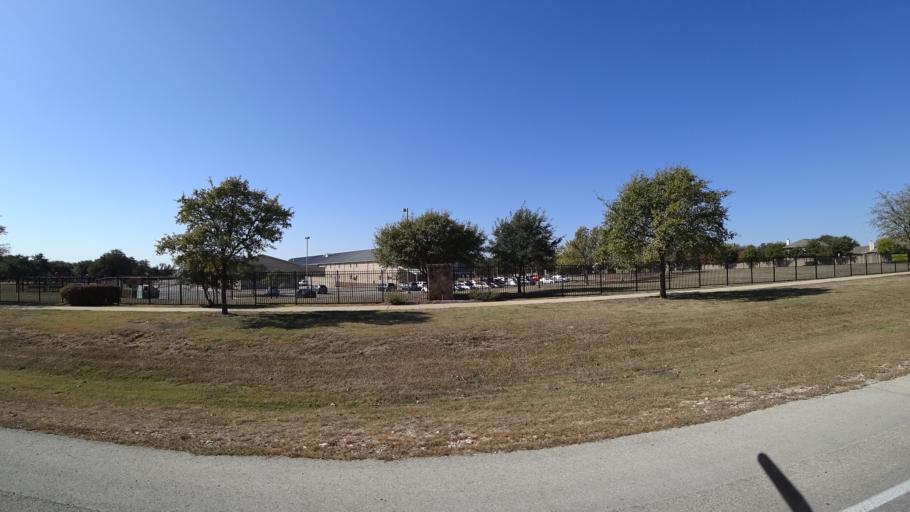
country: US
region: Texas
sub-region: Williamson County
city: Cedar Park
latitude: 30.4836
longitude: -97.8516
